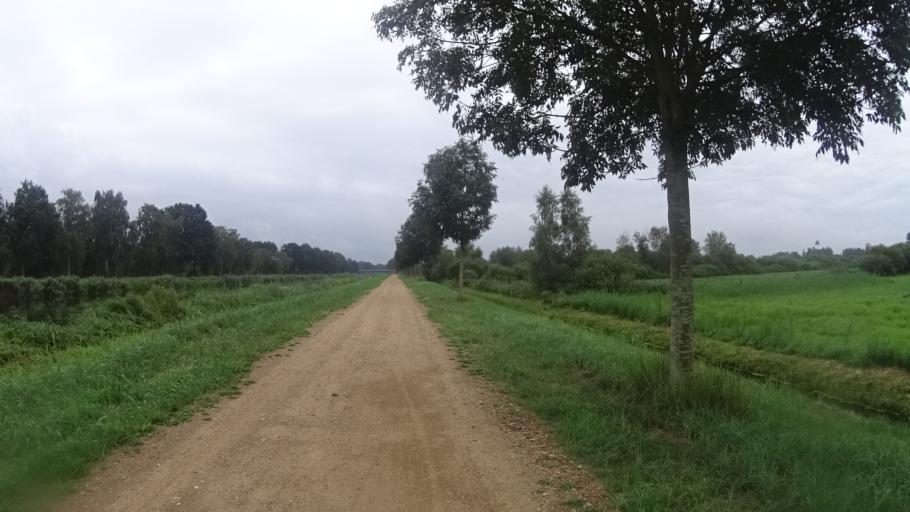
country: DE
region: Schleswig-Holstein
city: Buchen
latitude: 53.4863
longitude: 10.6303
